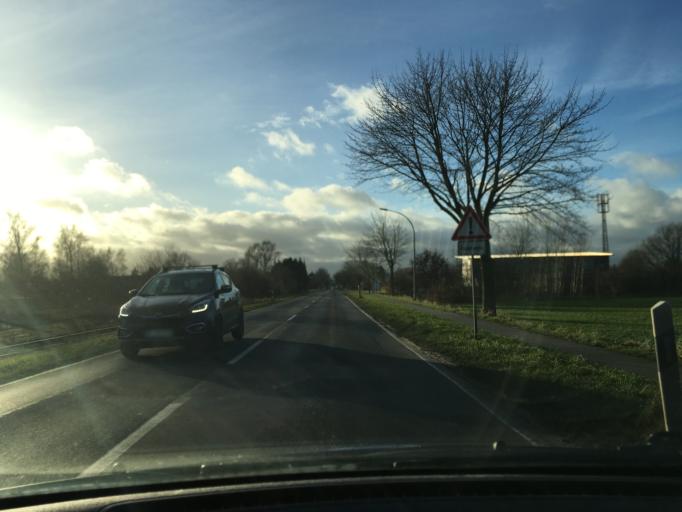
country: DE
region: Lower Saxony
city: Winsen
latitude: 53.3695
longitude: 10.2217
